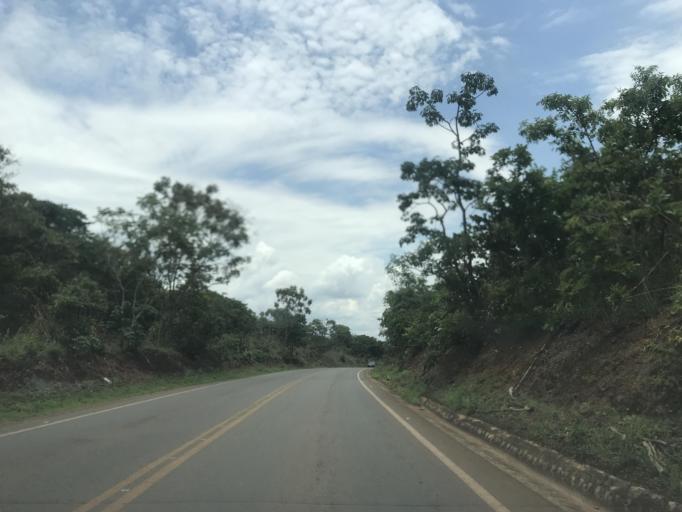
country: BR
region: Goias
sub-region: Vianopolis
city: Vianopolis
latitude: -16.7249
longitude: -48.4137
